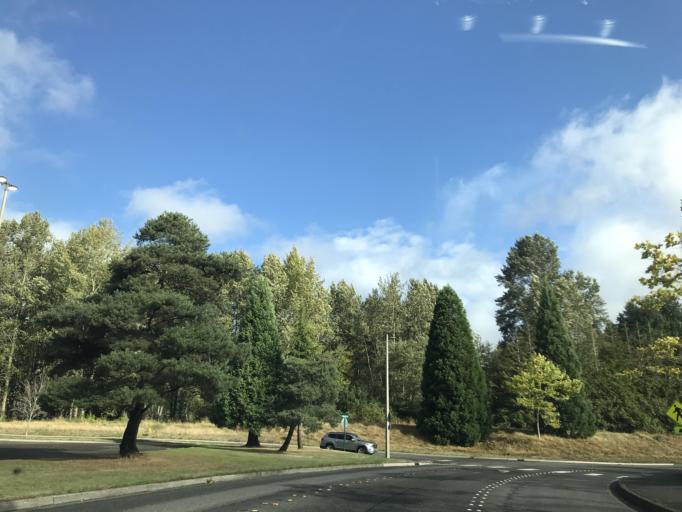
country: US
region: Washington
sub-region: Whatcom County
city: Bellingham
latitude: 48.7872
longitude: -122.4960
